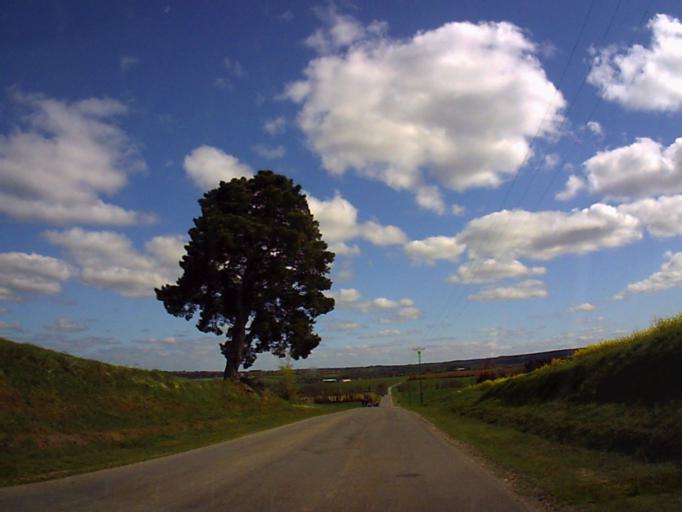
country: FR
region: Brittany
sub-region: Departement d'Ille-et-Vilaine
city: Boisgervilly
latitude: 48.1091
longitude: -2.1271
